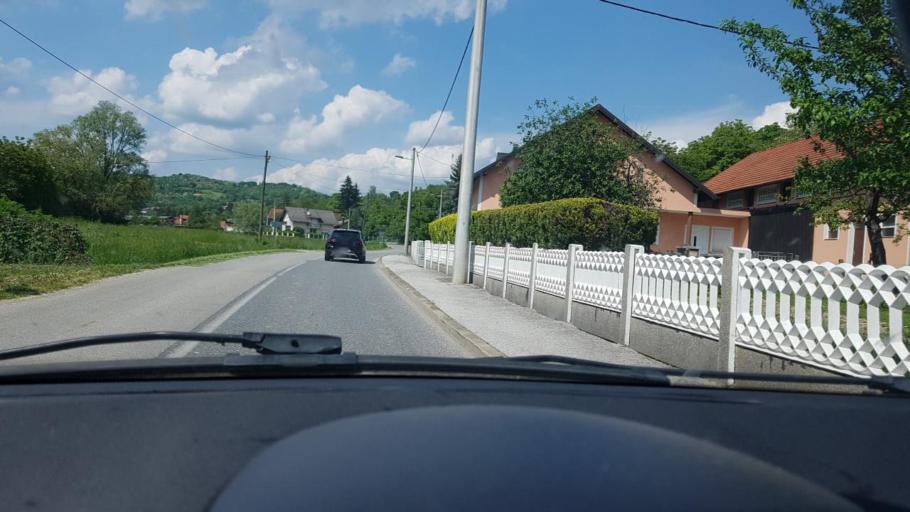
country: HR
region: Krapinsko-Zagorska
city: Marija Bistrica
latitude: 45.9240
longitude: 16.1709
